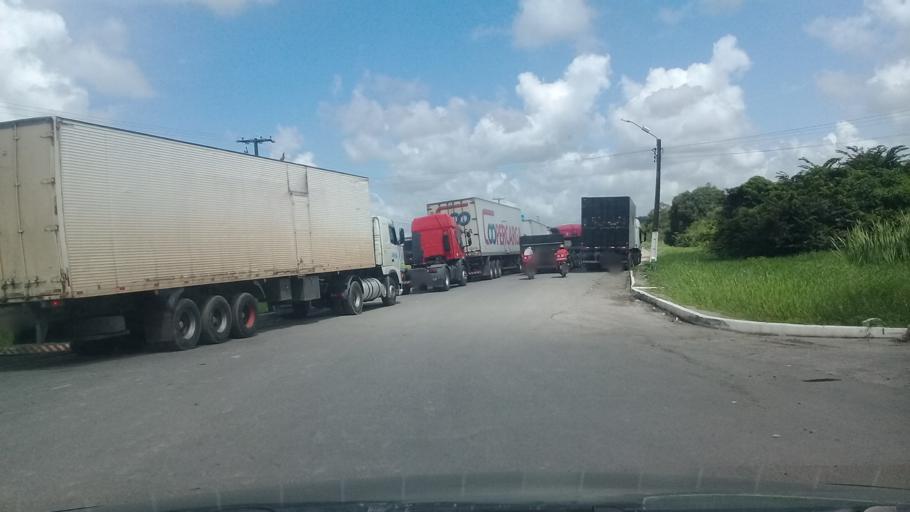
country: BR
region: Pernambuco
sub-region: Jaboatao Dos Guararapes
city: Jaboatao
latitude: -8.1774
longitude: -34.9500
